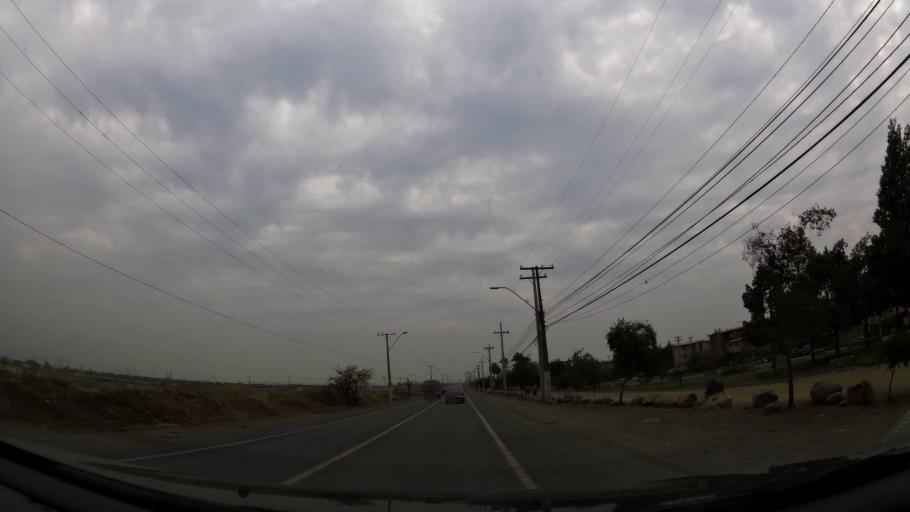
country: CL
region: Santiago Metropolitan
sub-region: Provincia de Chacabuco
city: Chicureo Abajo
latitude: -33.1928
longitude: -70.6644
